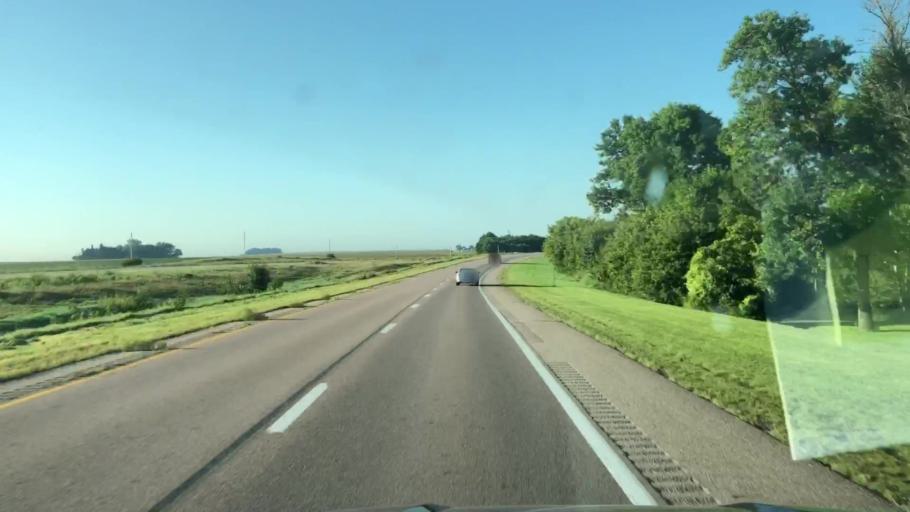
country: US
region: Iowa
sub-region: O'Brien County
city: Sheldon
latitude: 43.1351
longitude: -95.8809
